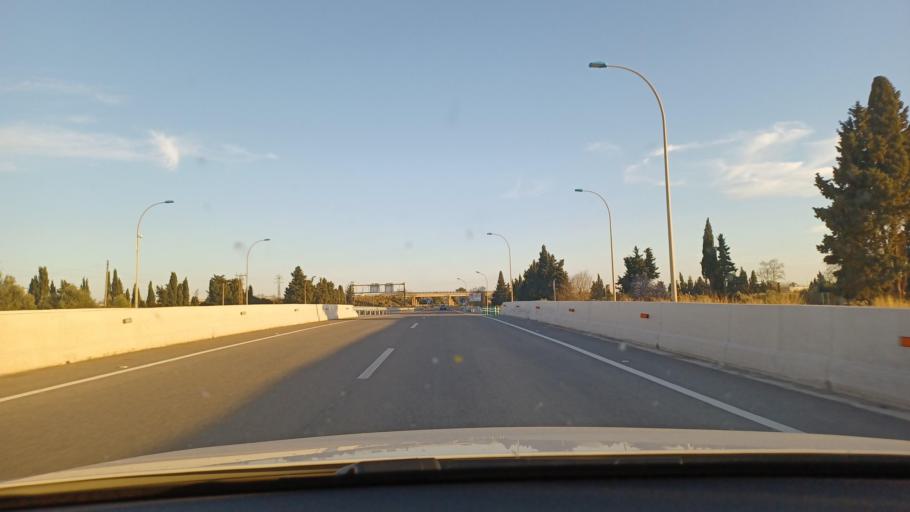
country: ES
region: Catalonia
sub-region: Provincia de Tarragona
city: Amposta
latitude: 40.7276
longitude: 0.5877
